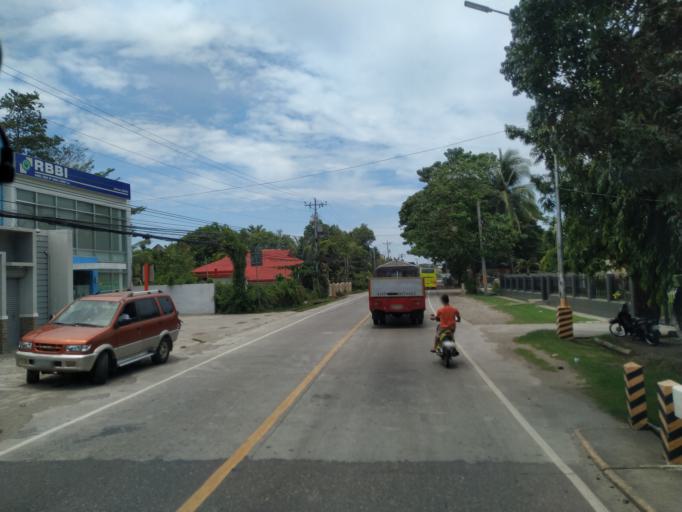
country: PH
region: Central Visayas
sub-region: Province of Negros Oriental
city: Sibulan
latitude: 9.3549
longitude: 123.2845
